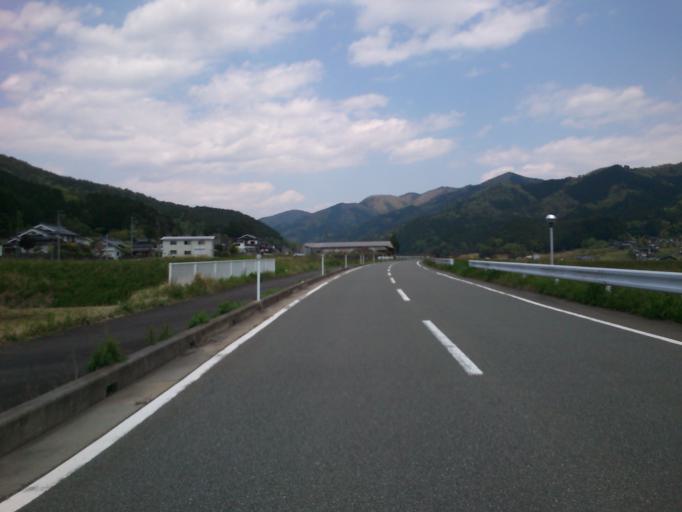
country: JP
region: Kyoto
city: Fukuchiyama
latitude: 35.3516
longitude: 134.9495
